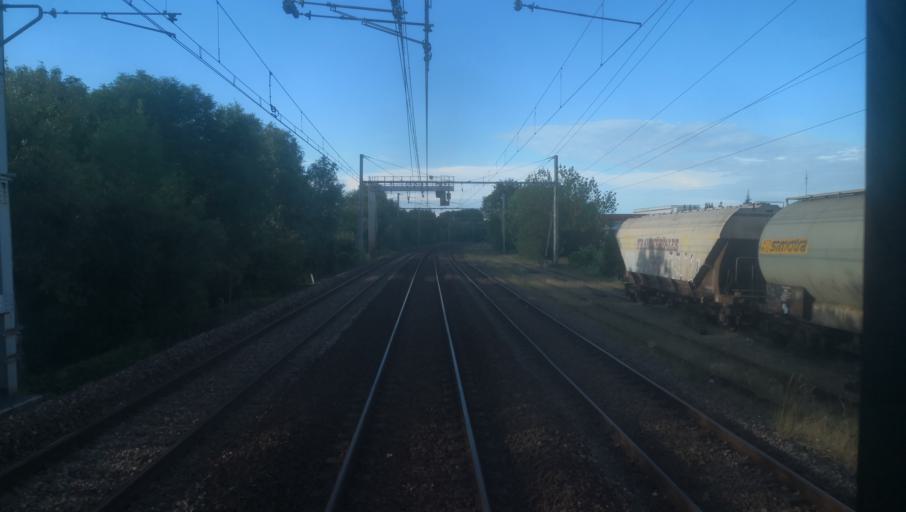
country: FR
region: Centre
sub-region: Departement de l'Indre
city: Issoudun
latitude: 46.9534
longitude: 1.9882
